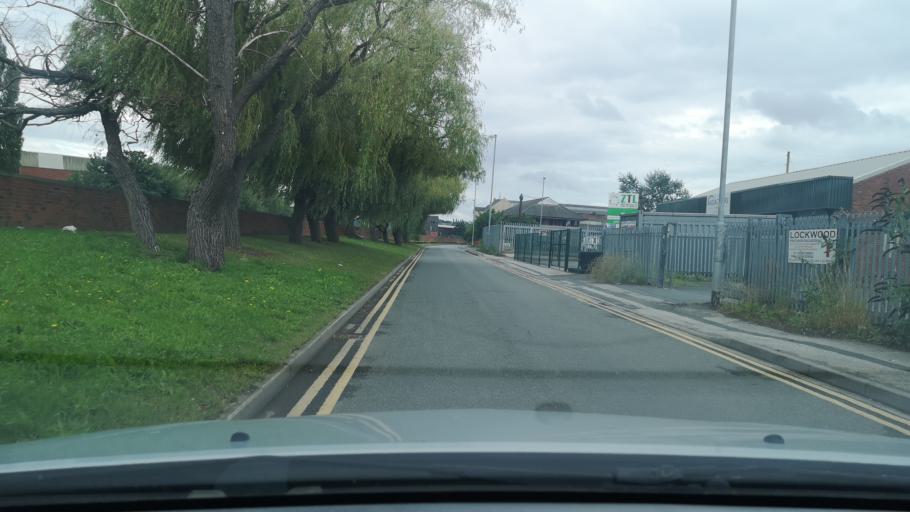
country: GB
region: England
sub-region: City and Borough of Wakefield
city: Wakefield
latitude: 53.6736
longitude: -1.4924
